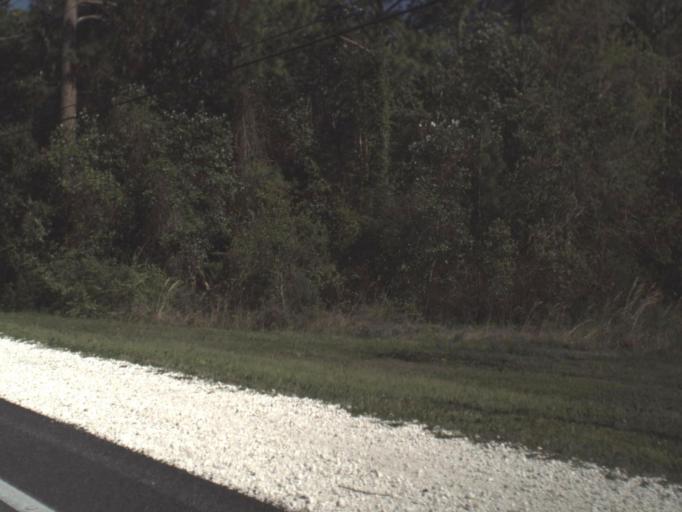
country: US
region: Florida
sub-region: Okaloosa County
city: Mary Esther
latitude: 30.4114
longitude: -86.7508
